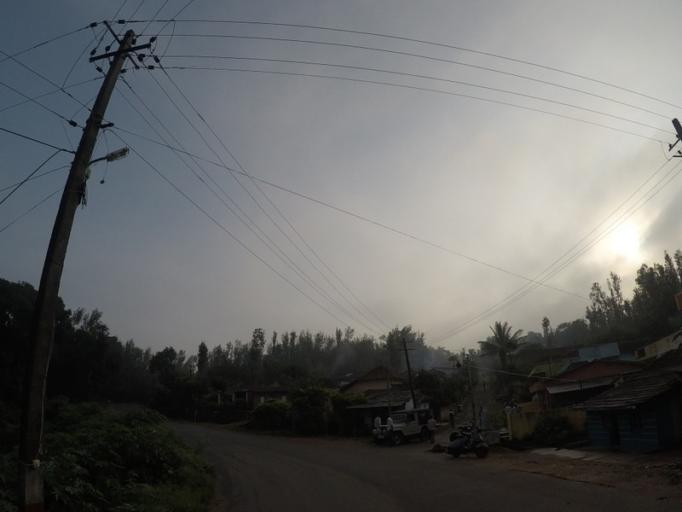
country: IN
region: Karnataka
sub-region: Chikmagalur
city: Chikmagalur
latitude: 13.3803
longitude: 75.7527
